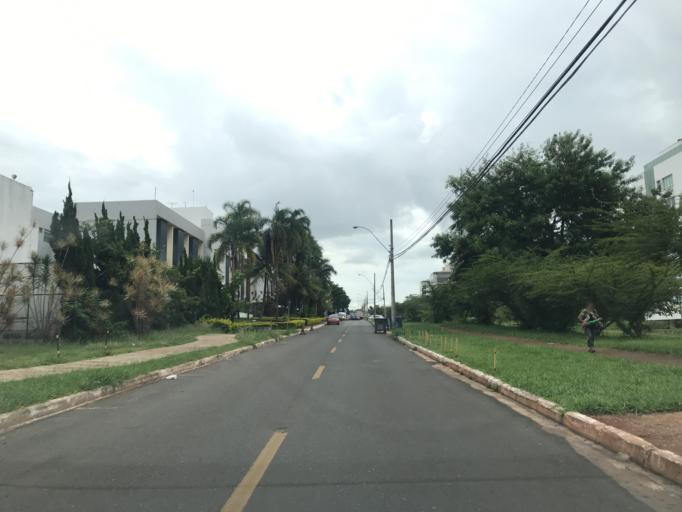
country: BR
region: Federal District
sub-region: Brasilia
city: Brasilia
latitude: -15.7912
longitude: -47.9192
